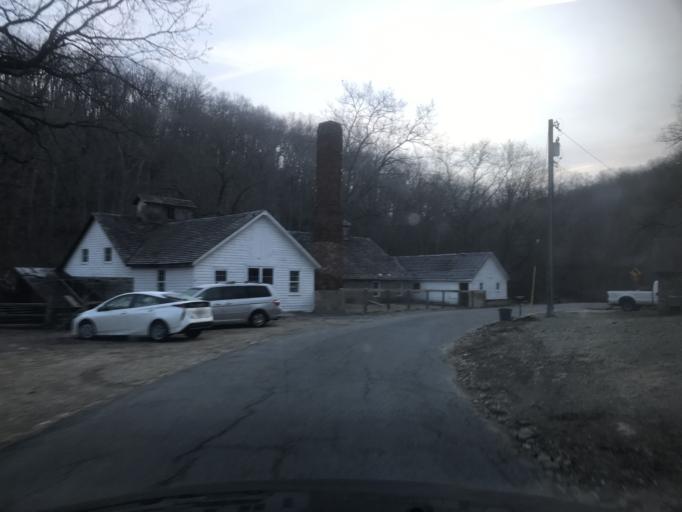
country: US
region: Pennsylvania
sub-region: York County
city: New Freedom
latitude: 39.6811
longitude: -76.6992
